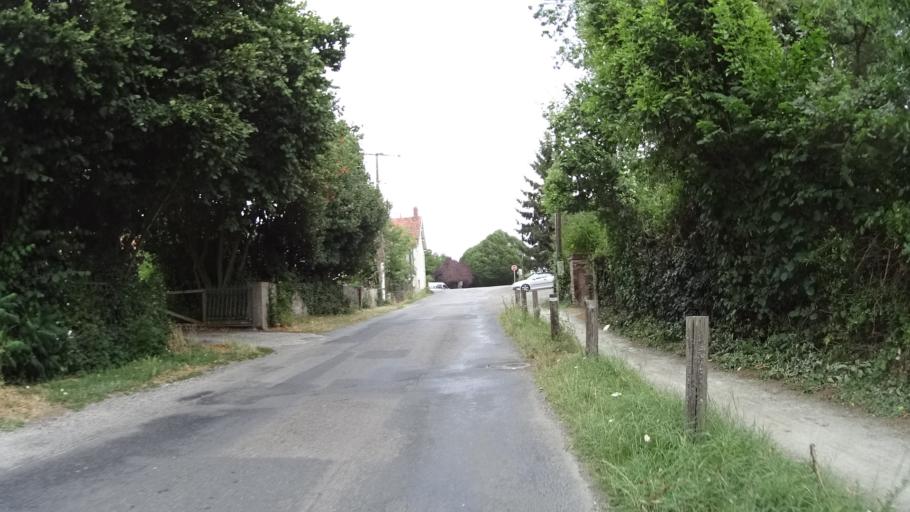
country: FR
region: Pays de la Loire
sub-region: Departement de la Loire-Atlantique
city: Oudon
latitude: 47.3444
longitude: -1.2922
